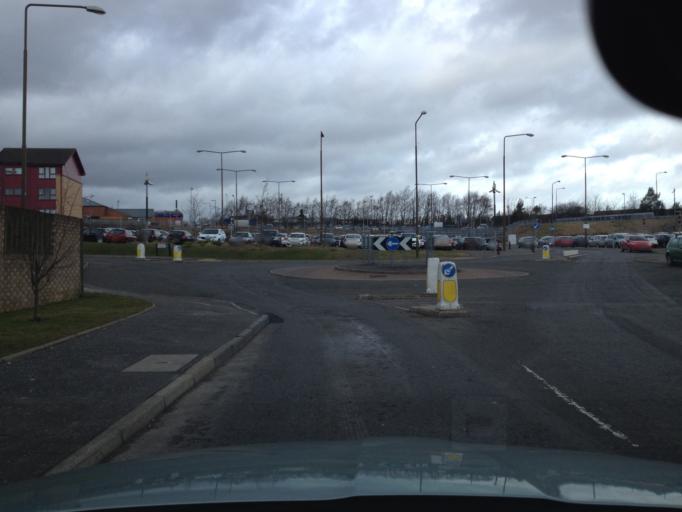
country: GB
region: Scotland
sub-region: West Lothian
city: Livingston
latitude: 55.9005
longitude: -3.5422
